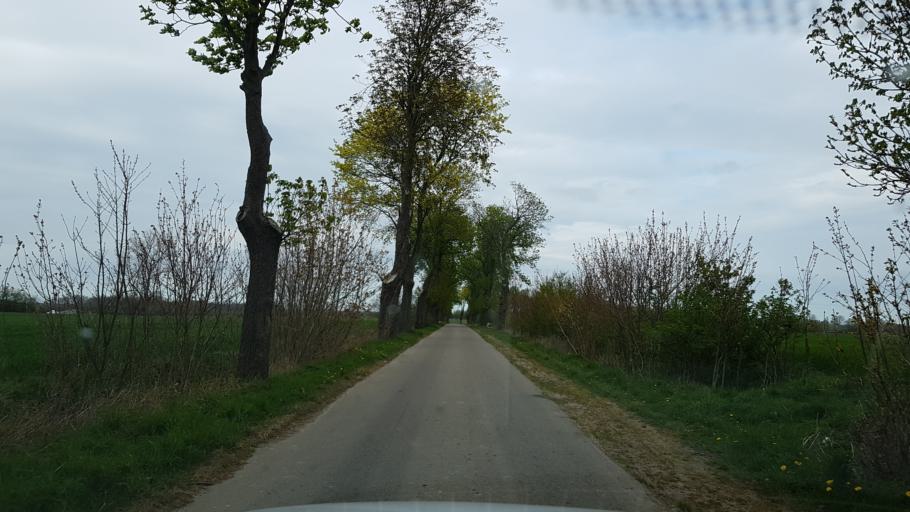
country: PL
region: West Pomeranian Voivodeship
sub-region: Powiat slawienski
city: Slawno
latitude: 54.5100
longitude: 16.5987
